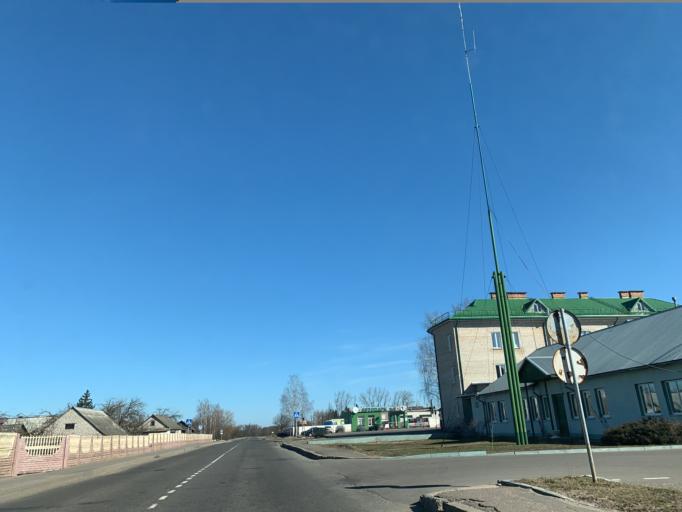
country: BY
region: Minsk
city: Nyasvizh
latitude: 53.2146
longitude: 26.6992
